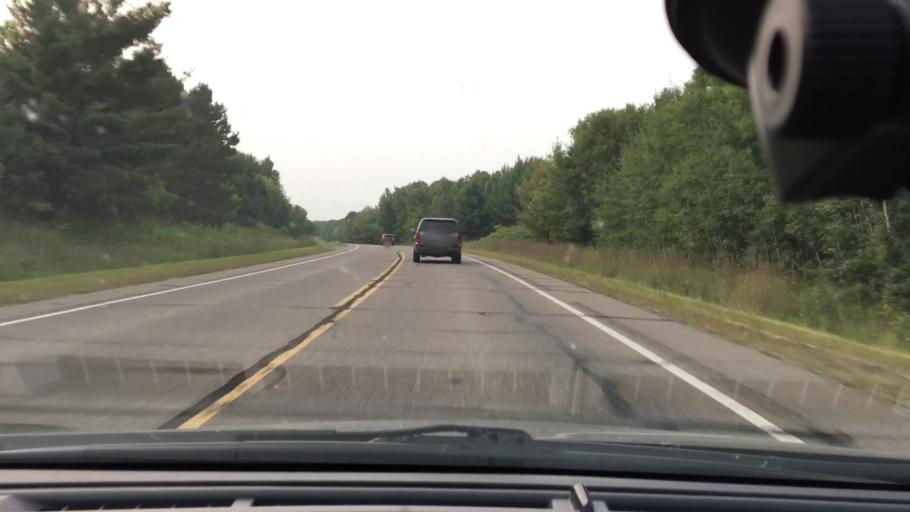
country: US
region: Minnesota
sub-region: Crow Wing County
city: Crosby
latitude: 46.4354
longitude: -93.8739
